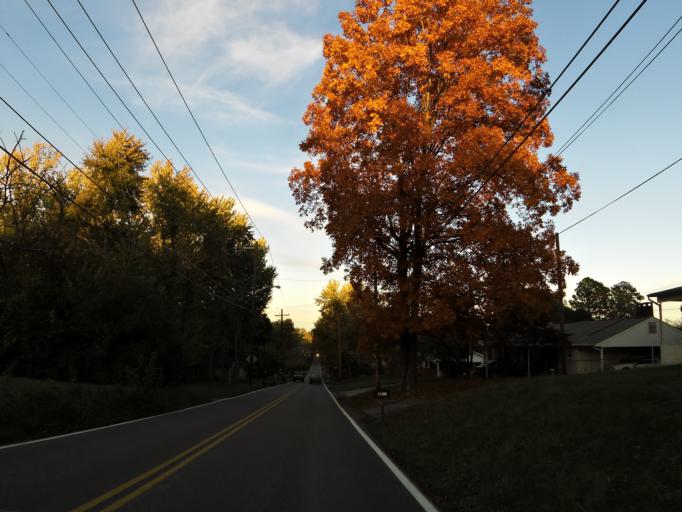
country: US
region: Tennessee
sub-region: Knox County
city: Knoxville
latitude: 35.9573
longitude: -83.9821
